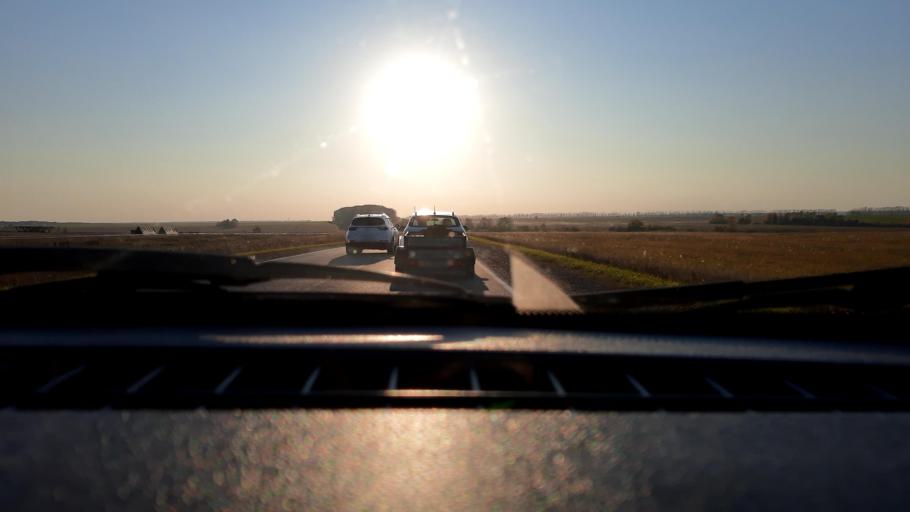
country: RU
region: Bashkortostan
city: Asanovo
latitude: 54.8261
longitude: 55.6316
